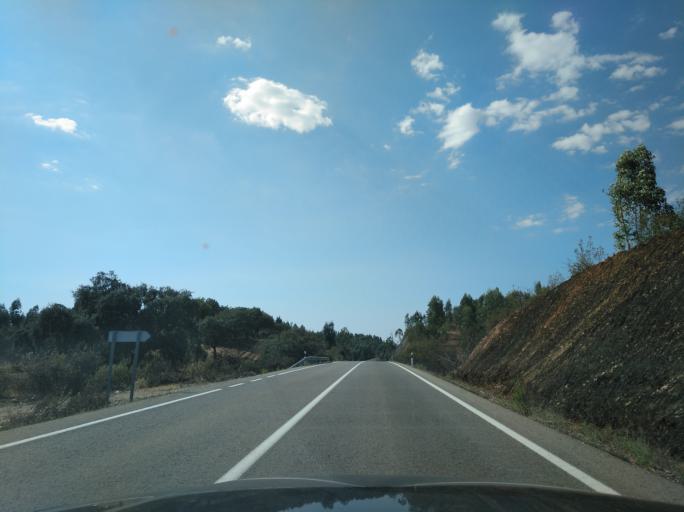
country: ES
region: Andalusia
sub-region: Provincia de Huelva
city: Santa Barbara de Casa
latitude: 37.8078
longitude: -7.2045
